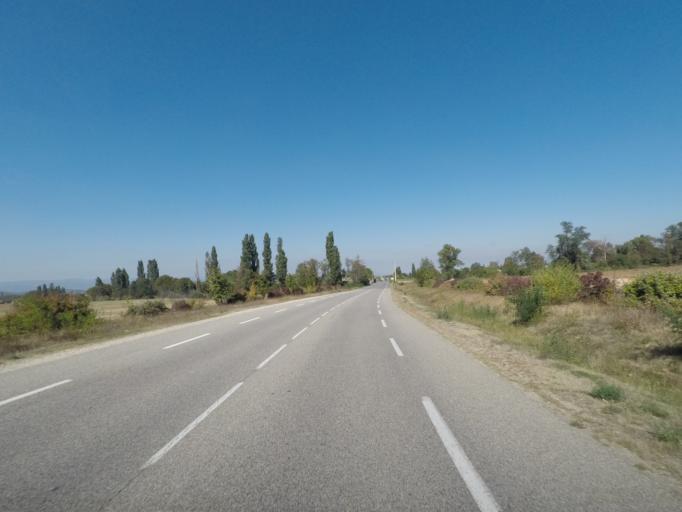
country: FR
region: Rhone-Alpes
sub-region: Departement de la Drome
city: Upie
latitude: 44.7947
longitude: 5.0193
